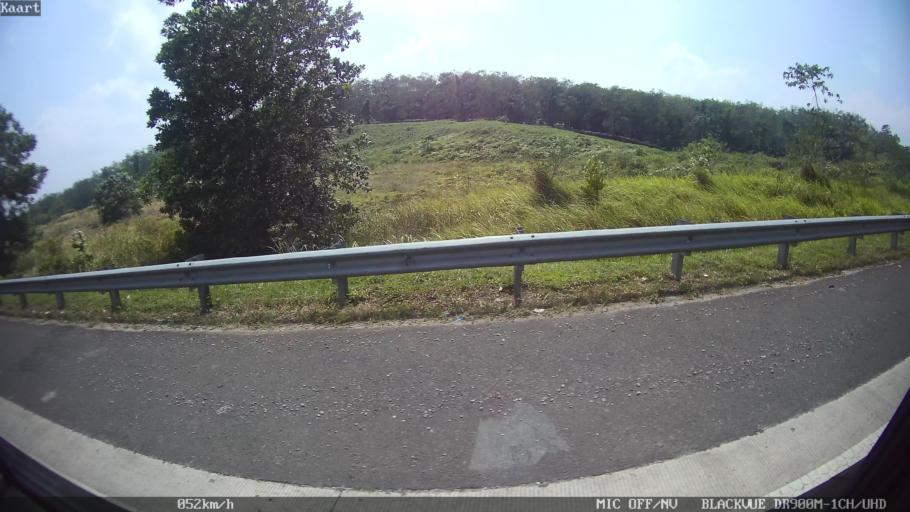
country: ID
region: Lampung
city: Kedaton
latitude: -5.3713
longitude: 105.3272
